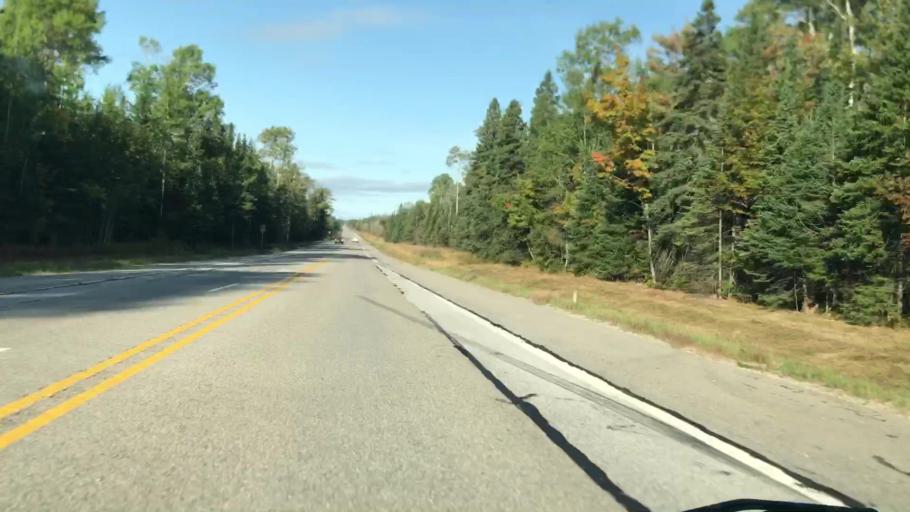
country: US
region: Michigan
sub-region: Luce County
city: Newberry
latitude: 46.3037
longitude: -85.2950
